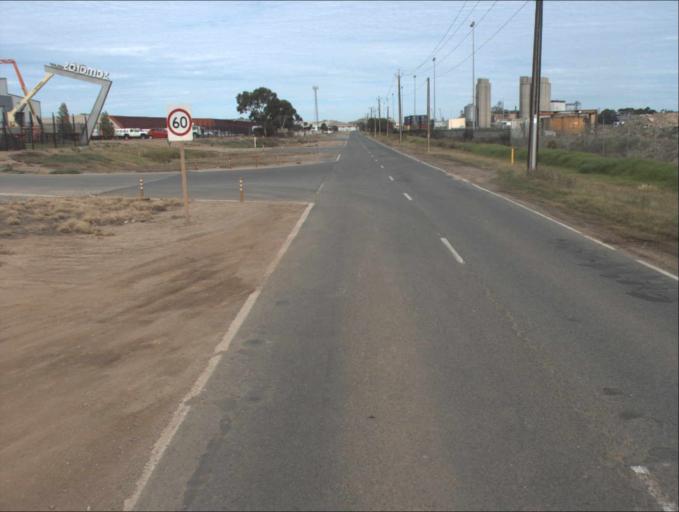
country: AU
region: South Australia
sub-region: Port Adelaide Enfield
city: Birkenhead
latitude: -34.8228
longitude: 138.5220
